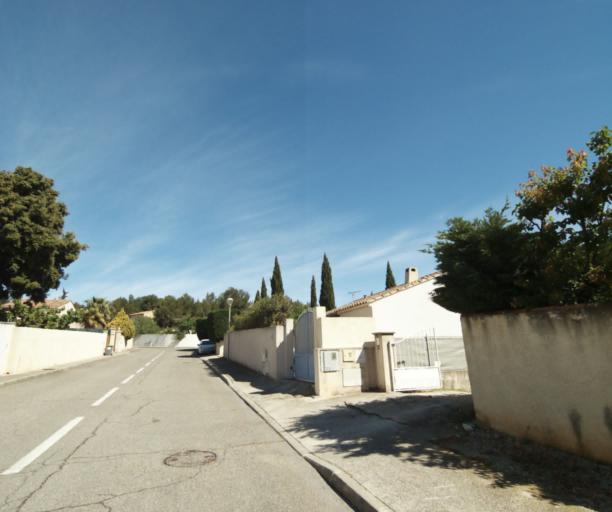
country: FR
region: Provence-Alpes-Cote d'Azur
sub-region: Departement des Bouches-du-Rhone
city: Rognac
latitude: 43.5110
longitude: 5.2105
